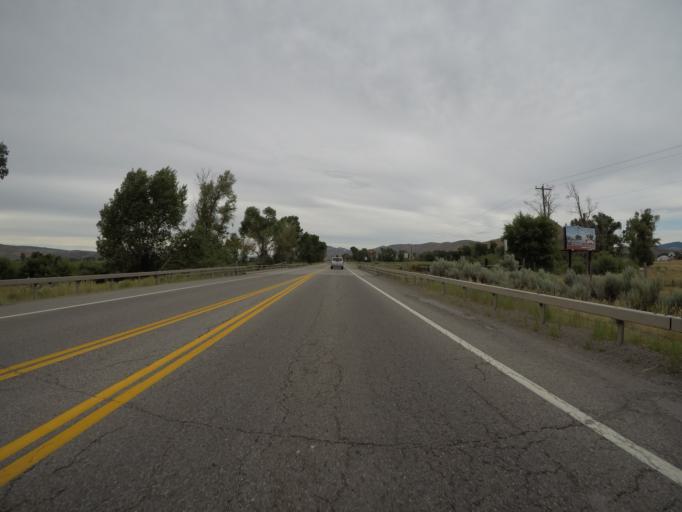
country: US
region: Idaho
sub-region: Bear Lake County
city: Montpelier
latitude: 42.0879
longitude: -110.9491
